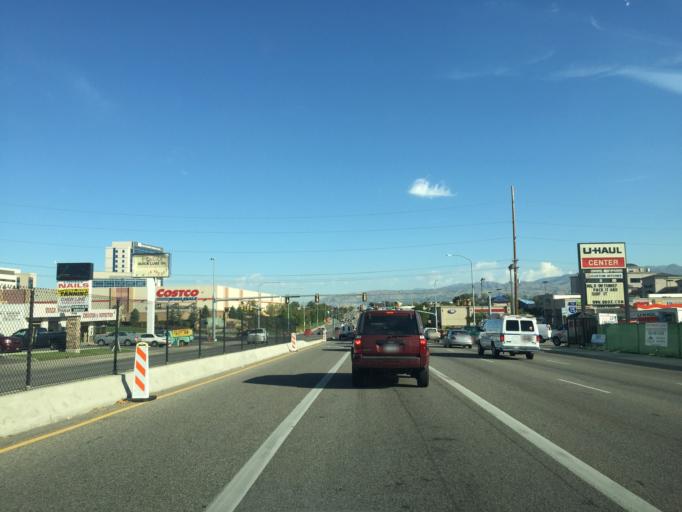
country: US
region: Utah
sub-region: Salt Lake County
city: Murray
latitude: 40.6550
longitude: -111.8883
